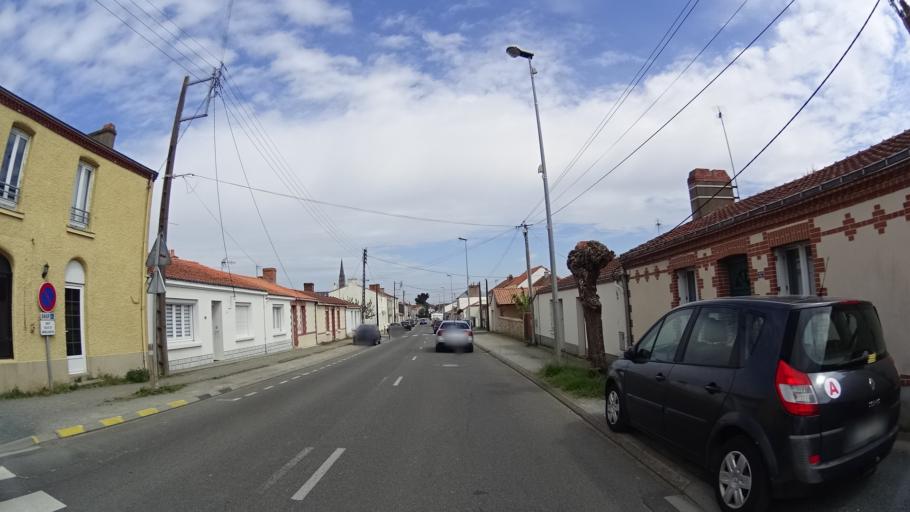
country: FR
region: Pays de la Loire
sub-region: Departement de la Loire-Atlantique
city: Sainte-Pazanne
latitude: 47.0994
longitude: -1.8151
